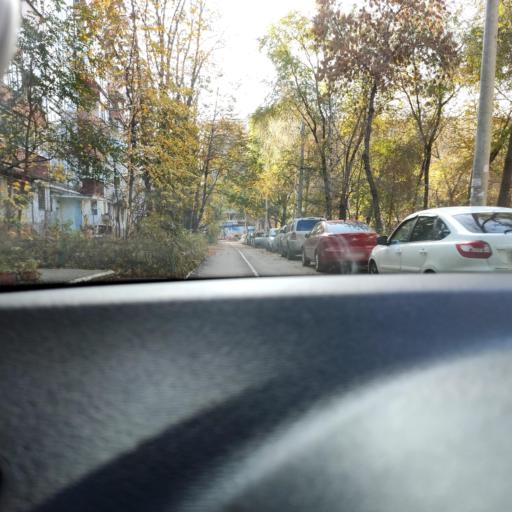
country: RU
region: Samara
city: Samara
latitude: 53.2101
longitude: 50.1431
